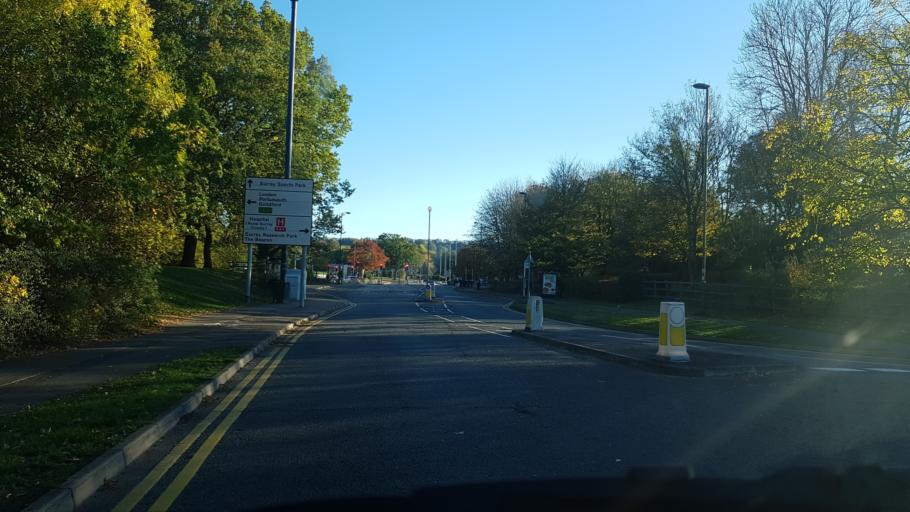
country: GB
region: England
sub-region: Surrey
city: Guildford
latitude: 51.2413
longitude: -0.6056
